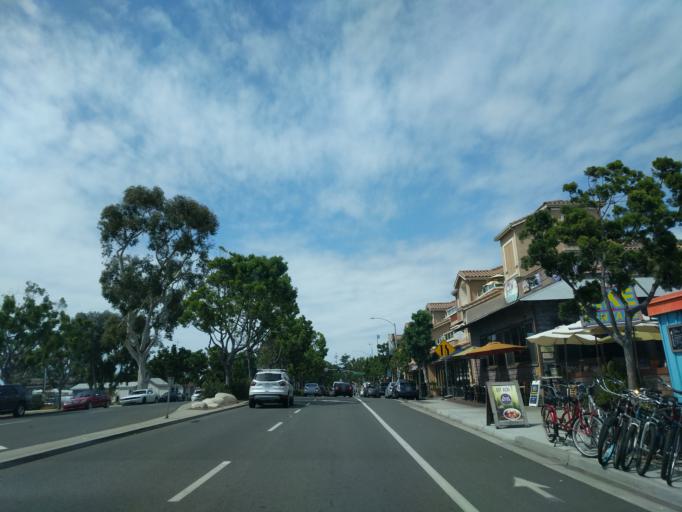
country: US
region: California
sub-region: San Diego County
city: Carlsbad
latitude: 33.1601
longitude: -117.3525
